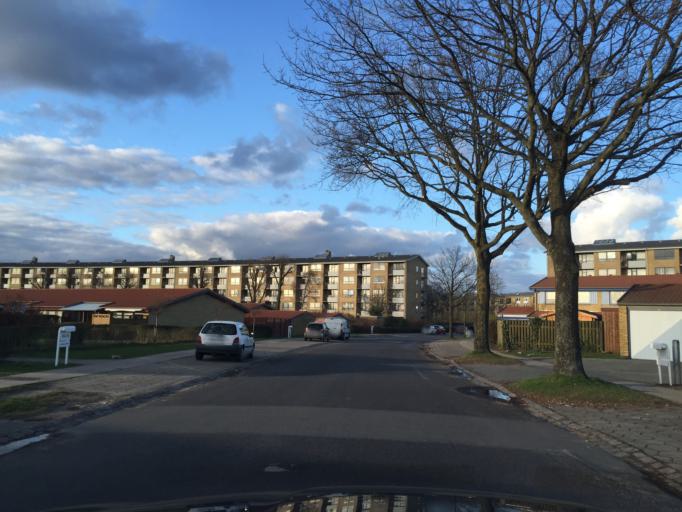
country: DK
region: South Denmark
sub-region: Odense Kommune
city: Neder Holluf
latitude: 55.3869
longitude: 10.4241
